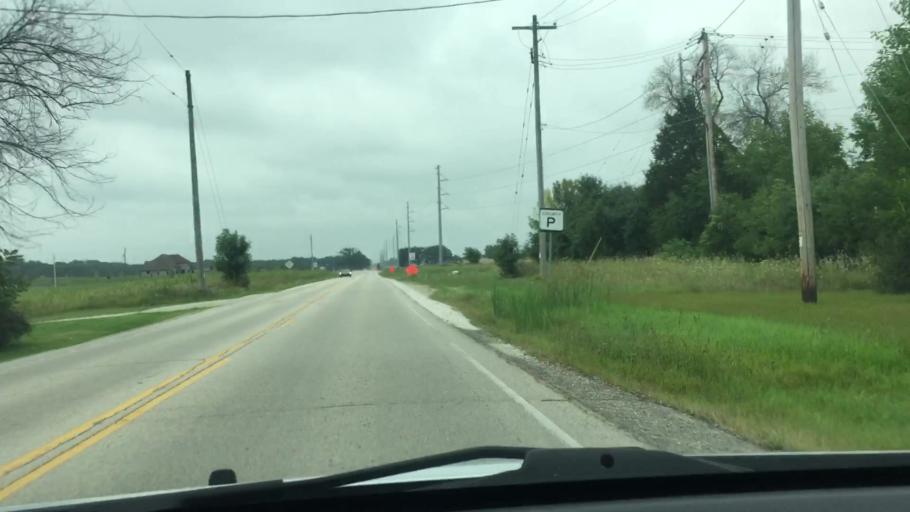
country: US
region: Wisconsin
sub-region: Waukesha County
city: Delafield
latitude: 43.0804
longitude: -88.4419
